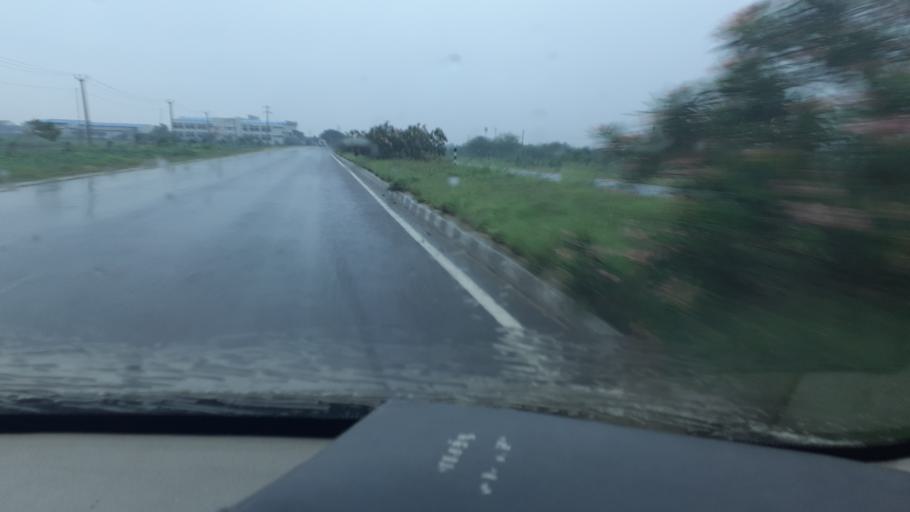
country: IN
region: Tamil Nadu
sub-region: Virudhunagar
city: Sattur
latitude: 9.4041
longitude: 77.9165
